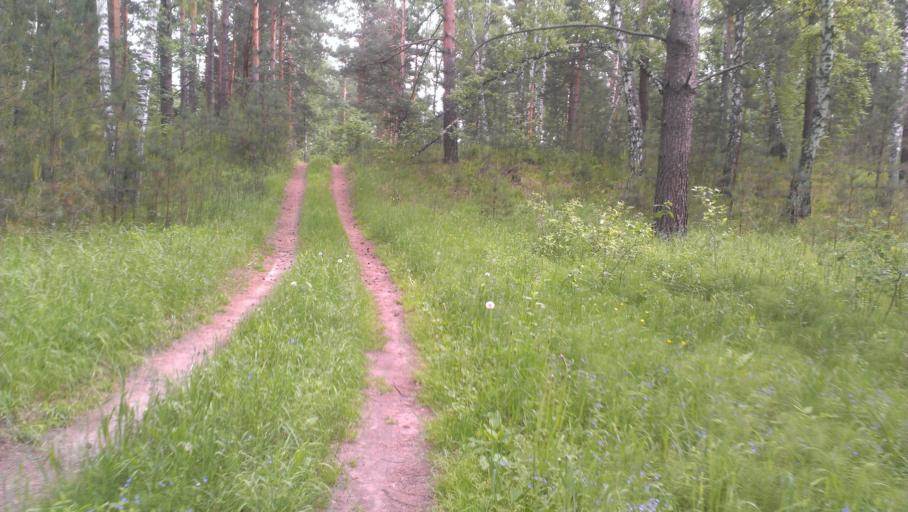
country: RU
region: Altai Krai
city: Sannikovo
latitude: 53.3478
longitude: 84.0395
